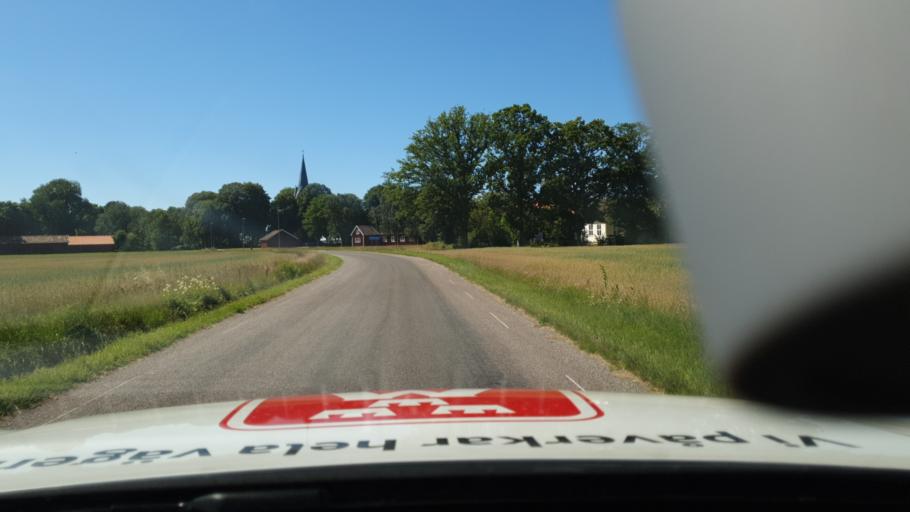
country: SE
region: Vaestra Goetaland
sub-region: Lidkopings Kommun
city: Vinninga
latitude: 58.3846
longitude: 13.2818
